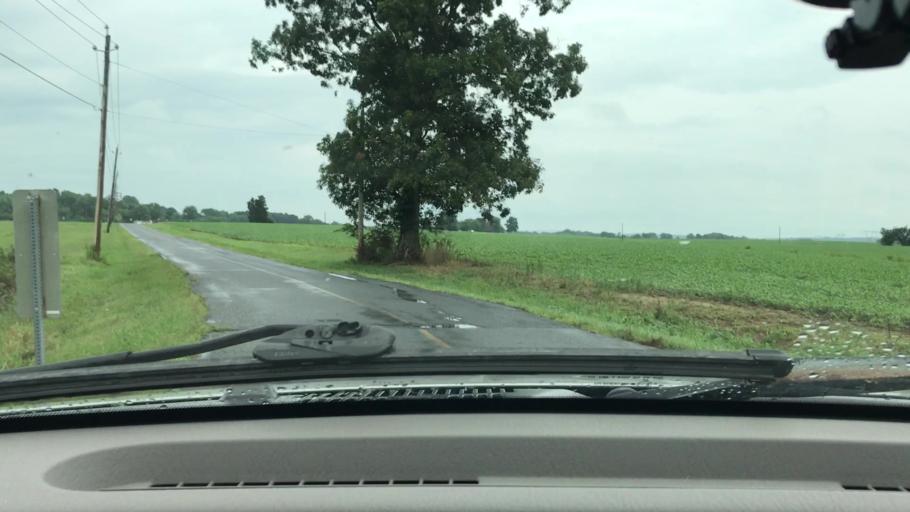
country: US
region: Pennsylvania
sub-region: Lancaster County
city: Elizabethtown
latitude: 40.1937
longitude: -76.6108
